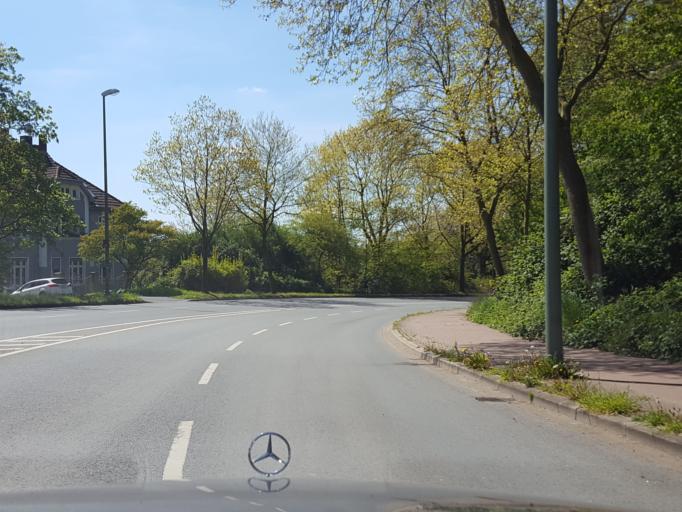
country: DE
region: North Rhine-Westphalia
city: Witten
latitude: 51.4807
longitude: 7.3261
